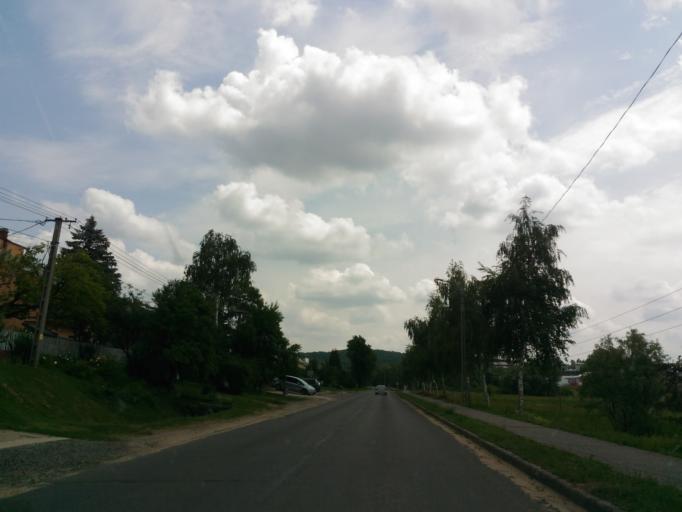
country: HU
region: Baranya
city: Komlo
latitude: 46.1910
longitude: 18.2348
